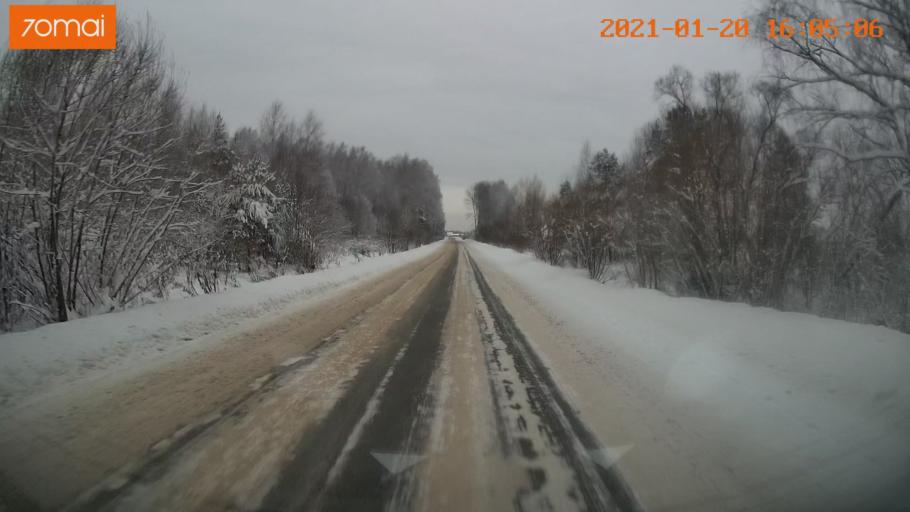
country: RU
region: Vladimir
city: Sudogda
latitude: 56.0626
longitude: 40.8101
